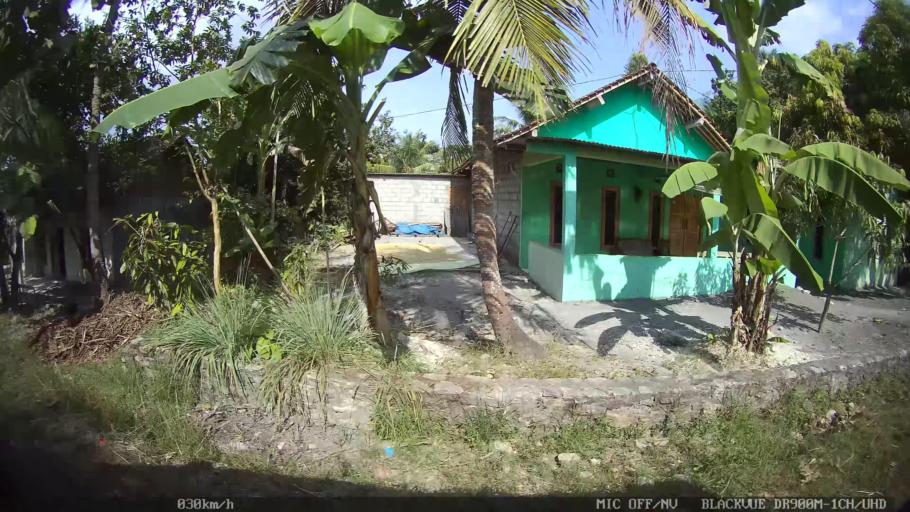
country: ID
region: Daerah Istimewa Yogyakarta
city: Kasihan
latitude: -7.8477
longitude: 110.3004
